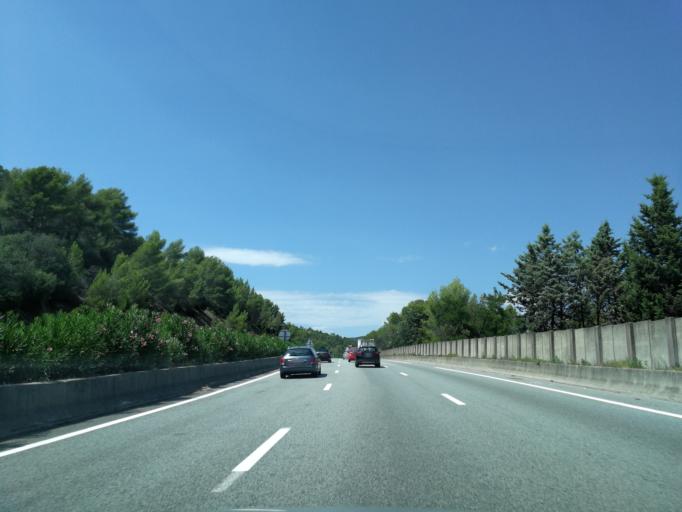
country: FR
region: Provence-Alpes-Cote d'Azur
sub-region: Departement du Var
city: Frejus
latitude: 43.4790
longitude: 6.7418
